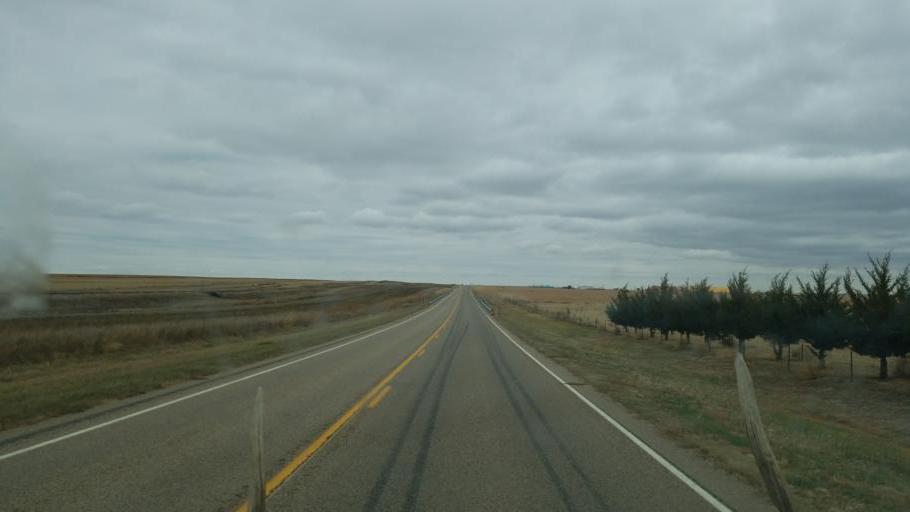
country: US
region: Colorado
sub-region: Cheyenne County
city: Cheyenne Wells
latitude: 38.8296
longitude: -102.3072
